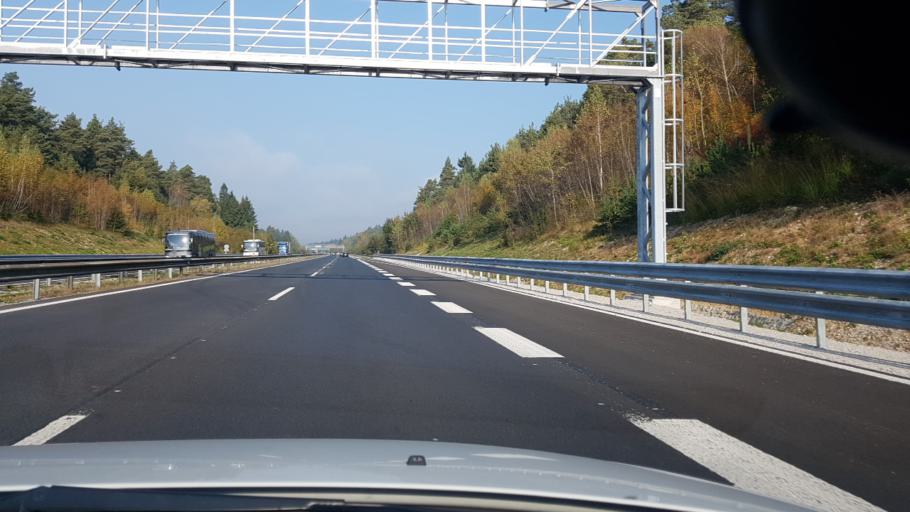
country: SI
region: Vodice
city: Vodice
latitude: 46.1979
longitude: 14.4696
